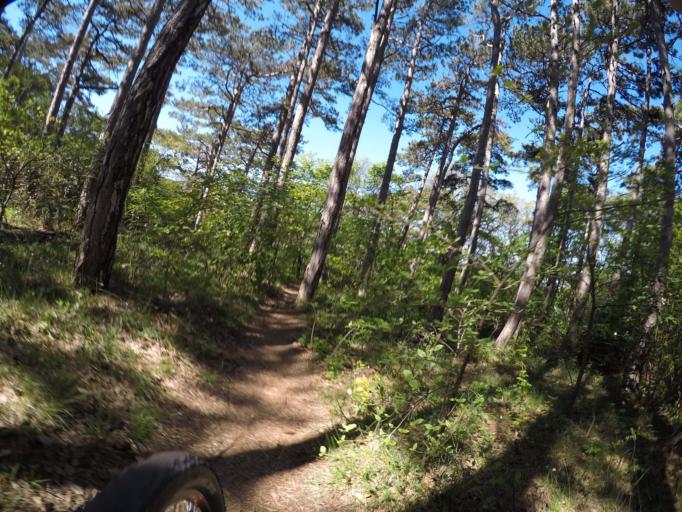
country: AT
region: Lower Austria
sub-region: Politischer Bezirk Modling
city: Modling
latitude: 48.0691
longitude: 16.2810
